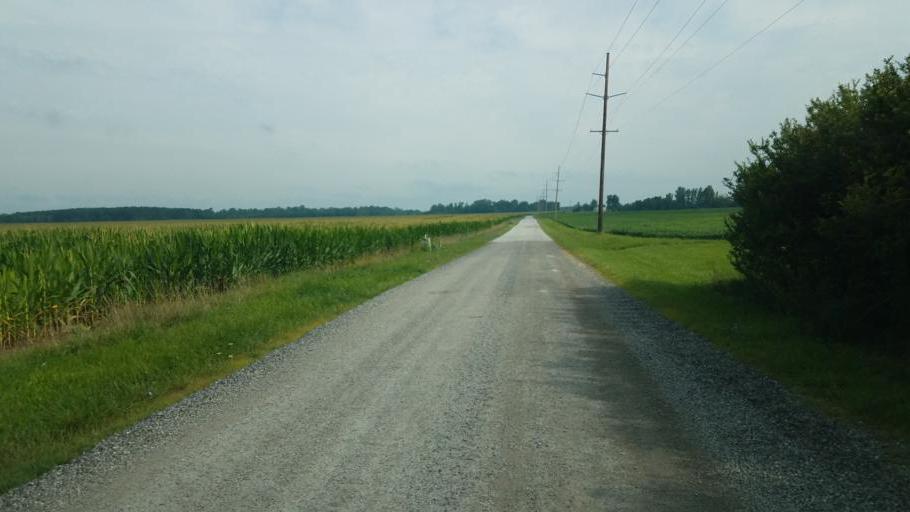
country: US
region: Ohio
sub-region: Delaware County
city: Ashley
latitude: 40.3756
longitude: -82.9111
